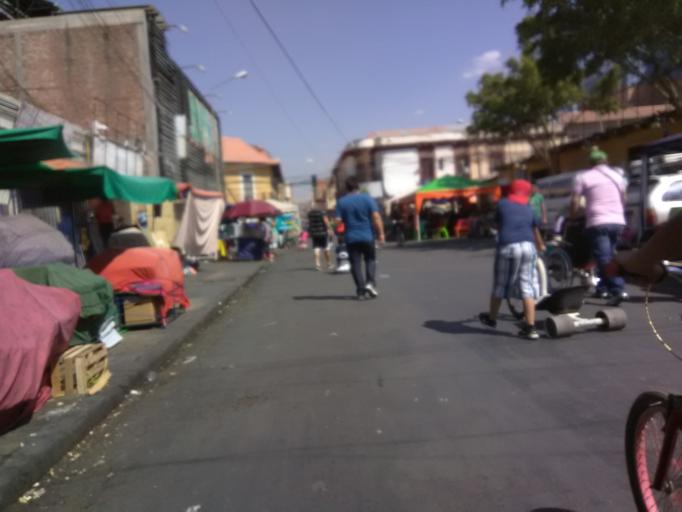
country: BO
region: Cochabamba
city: Cochabamba
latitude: -17.3946
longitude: -66.1551
